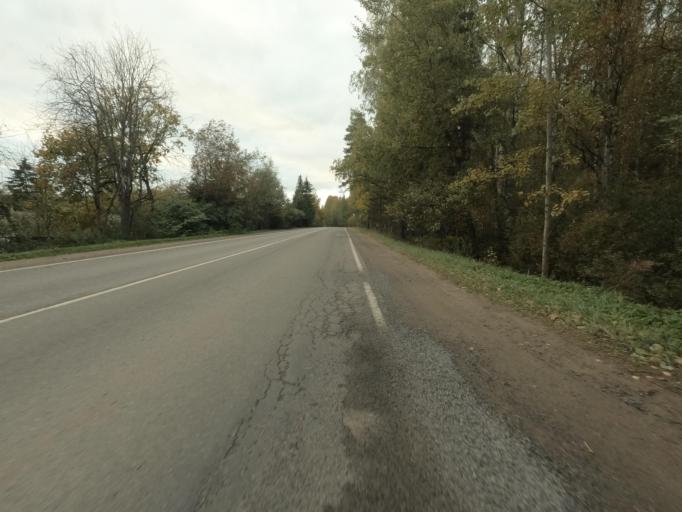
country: RU
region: Leningrad
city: Pavlovo
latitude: 59.7894
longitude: 30.9619
